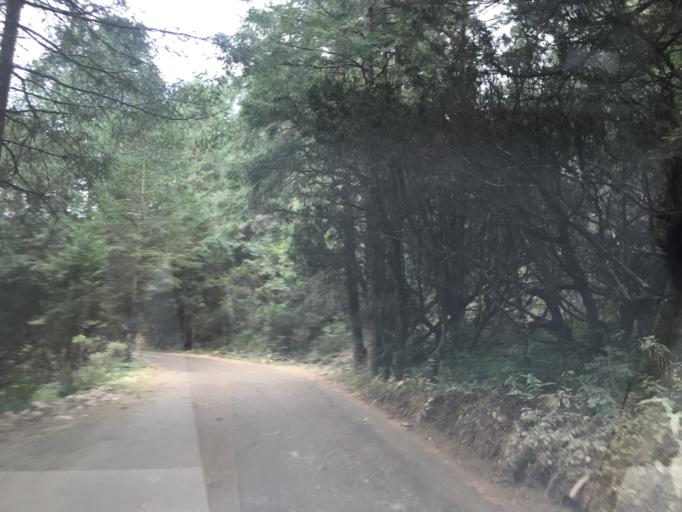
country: MX
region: Michoacan
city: Mineral de Angangueo
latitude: 19.6618
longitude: -100.2714
